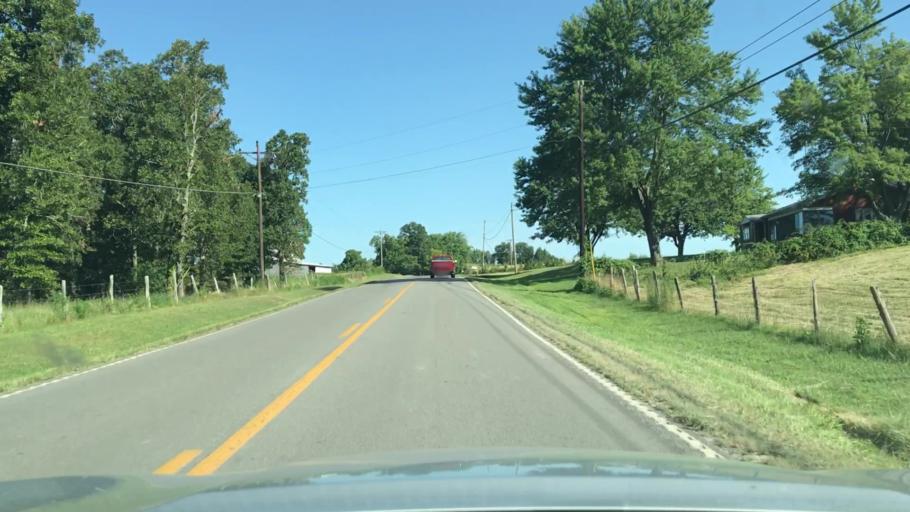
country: US
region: Kentucky
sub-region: Muhlenberg County
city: Greenville
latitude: 37.1706
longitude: -87.1504
